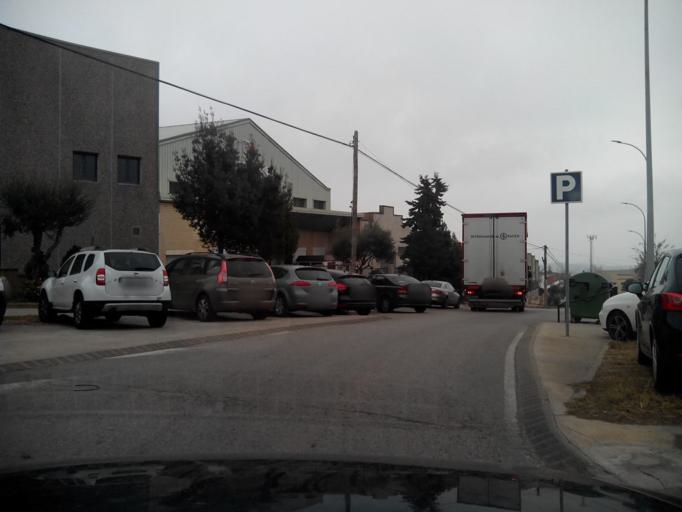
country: ES
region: Catalonia
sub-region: Provincia de Barcelona
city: Berga
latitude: 42.0918
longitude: 1.8242
